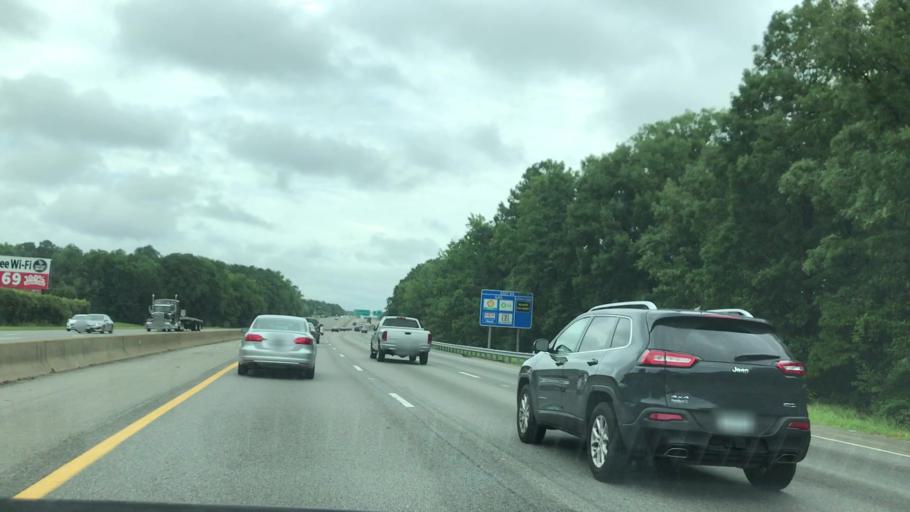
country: US
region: Virginia
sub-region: Chesterfield County
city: Bellwood
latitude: 37.3940
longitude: -77.4233
